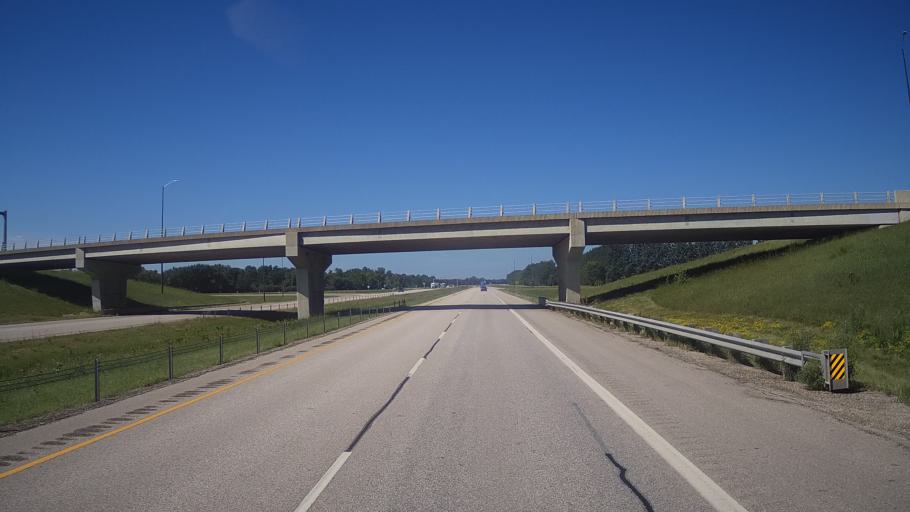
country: CA
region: Manitoba
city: Portage la Prairie
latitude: 49.9547
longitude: -98.2733
